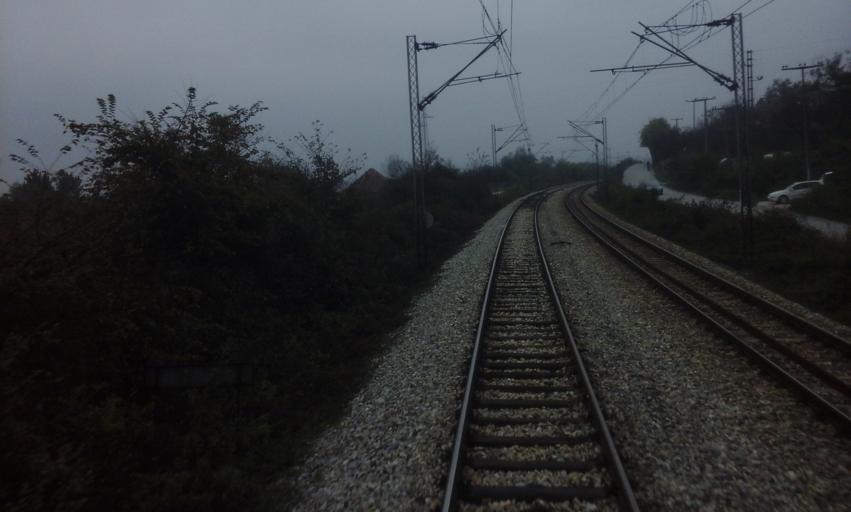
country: RS
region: Central Serbia
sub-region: Pomoravski Okrug
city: Jagodina
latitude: 44.0025
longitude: 21.2359
